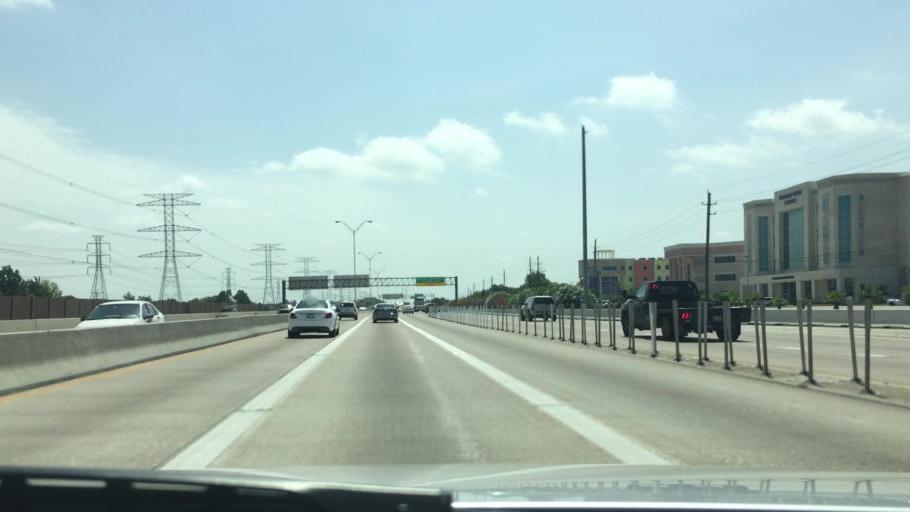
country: US
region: Texas
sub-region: Harris County
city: Hudson
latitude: 29.9376
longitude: -95.4679
